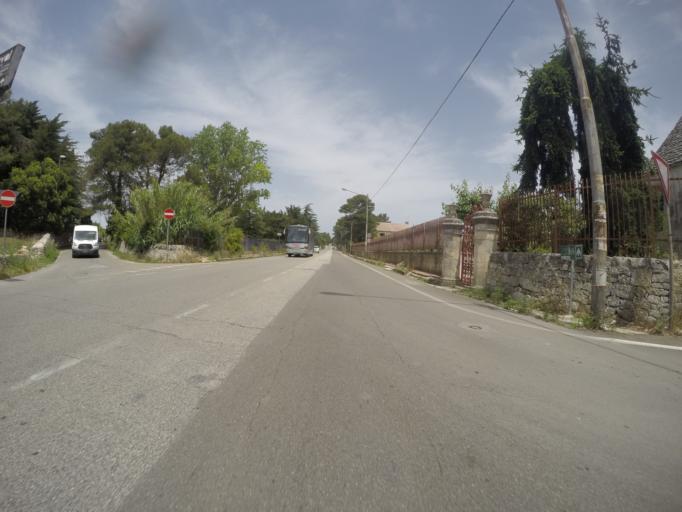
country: IT
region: Apulia
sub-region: Provincia di Taranto
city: Martina Franca
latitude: 40.6897
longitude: 17.3341
